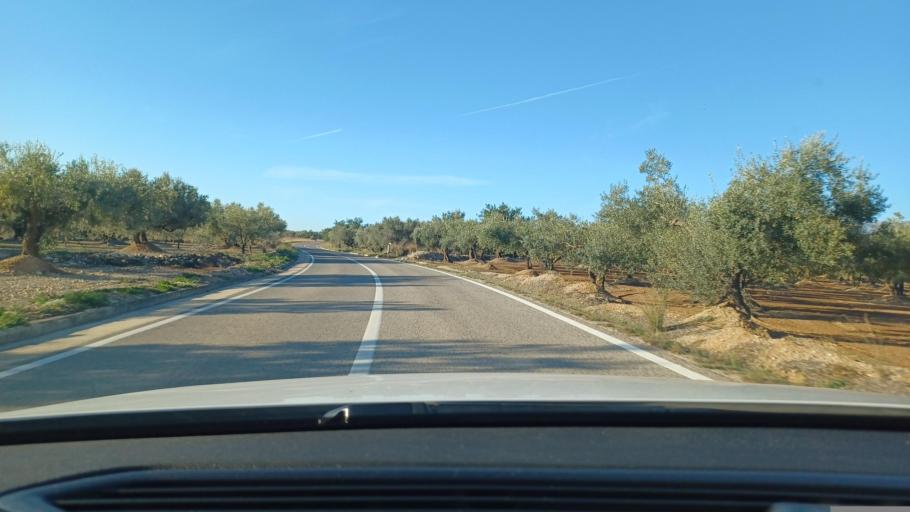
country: ES
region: Catalonia
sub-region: Provincia de Tarragona
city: Mas de Barberans
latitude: 40.7191
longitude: 0.4234
